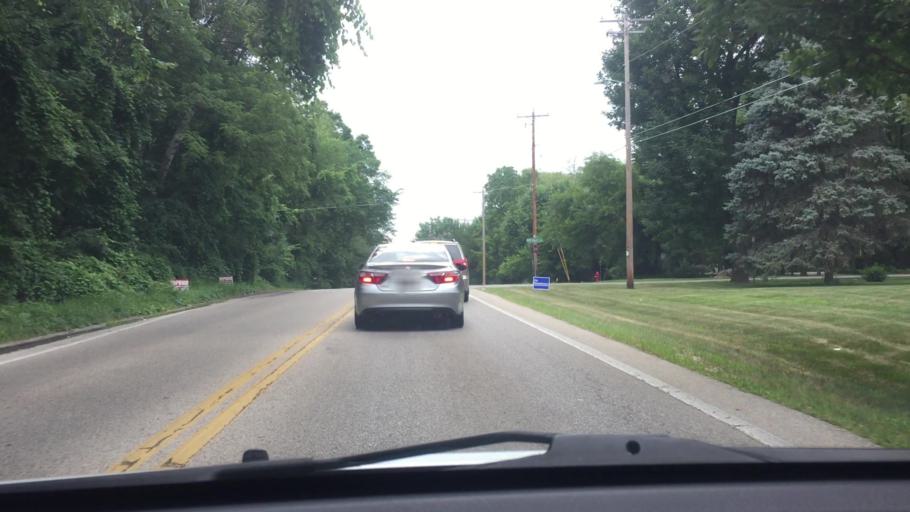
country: US
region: Wisconsin
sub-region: Waukesha County
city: Brookfield
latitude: 43.0605
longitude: -88.0994
